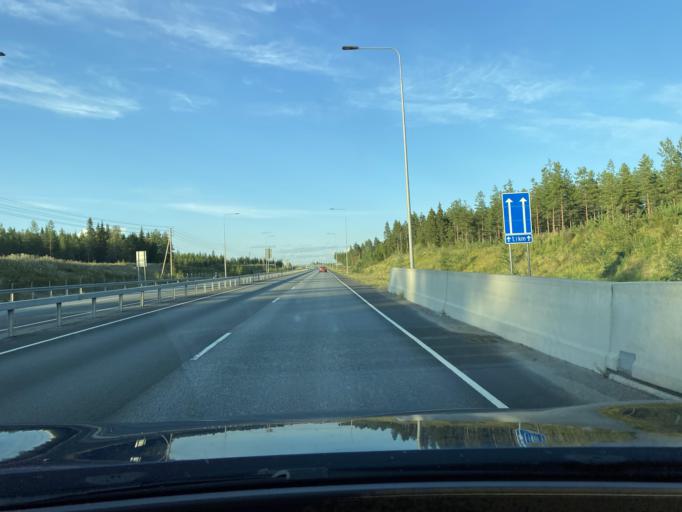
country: FI
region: Southern Ostrobothnia
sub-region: Seinaejoki
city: Seinaejoki
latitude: 62.7339
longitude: 22.9005
